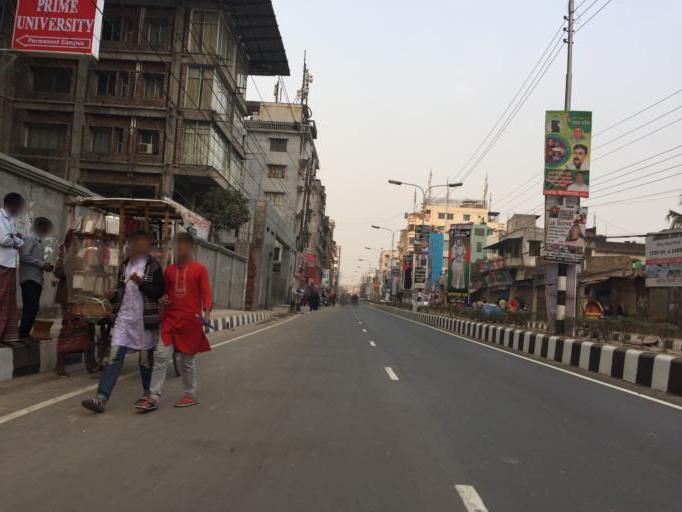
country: BD
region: Dhaka
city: Azimpur
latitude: 23.7902
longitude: 90.3482
